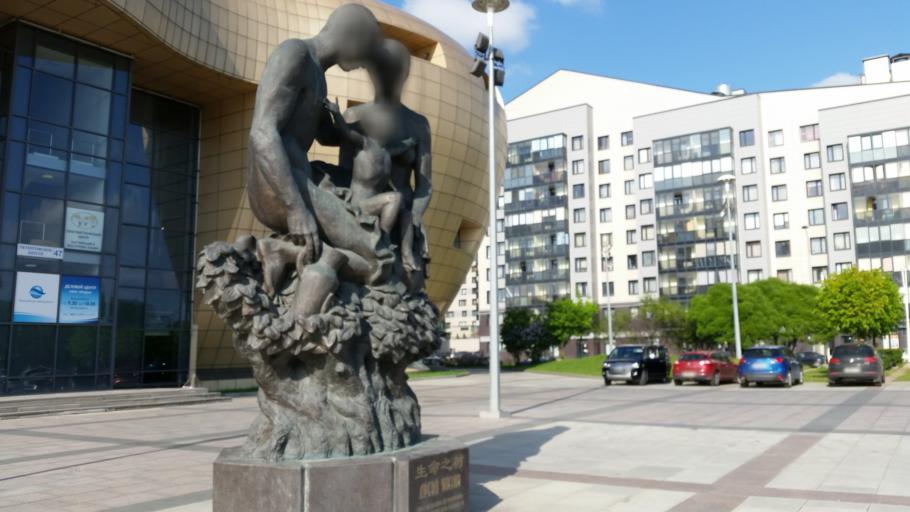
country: RU
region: St.-Petersburg
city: Sosnovaya Polyana
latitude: 59.8482
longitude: 30.1487
